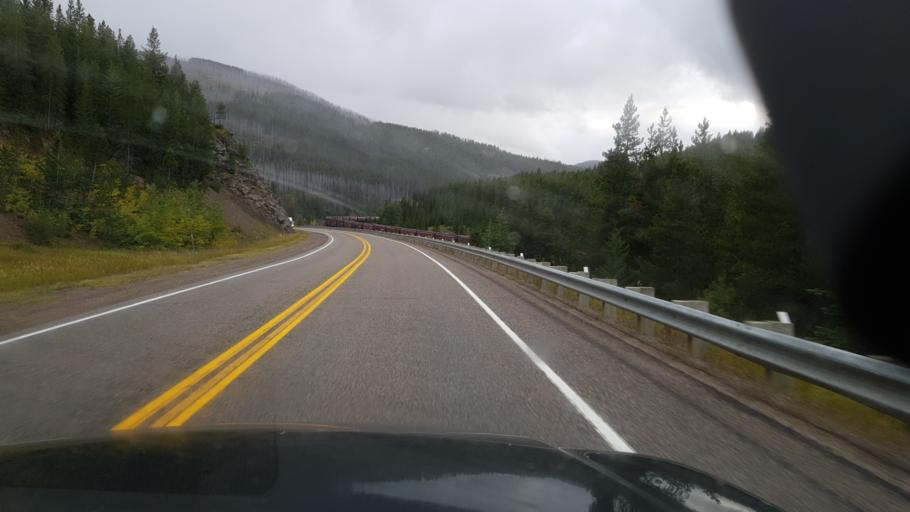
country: US
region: Montana
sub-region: Glacier County
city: South Browning
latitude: 48.3076
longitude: -113.3633
